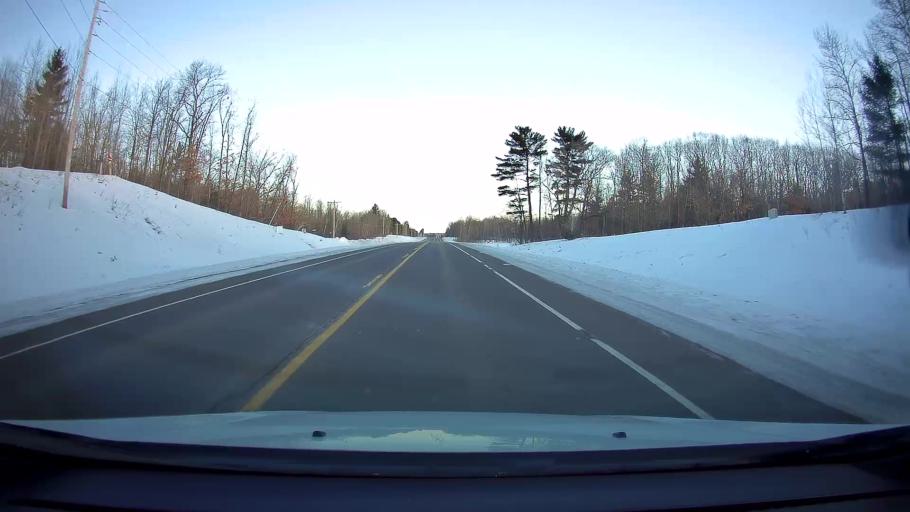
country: US
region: Wisconsin
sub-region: Barron County
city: Cumberland
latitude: 45.5845
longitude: -92.0176
